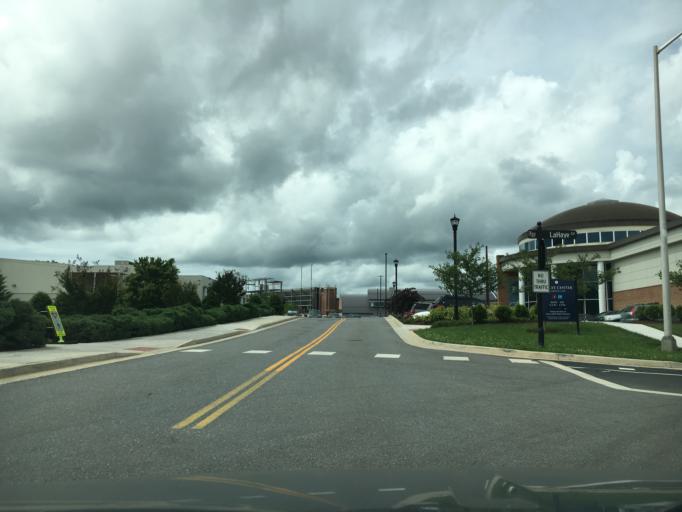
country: US
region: Virginia
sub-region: City of Lynchburg
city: West Lynchburg
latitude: 37.3579
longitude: -79.1722
